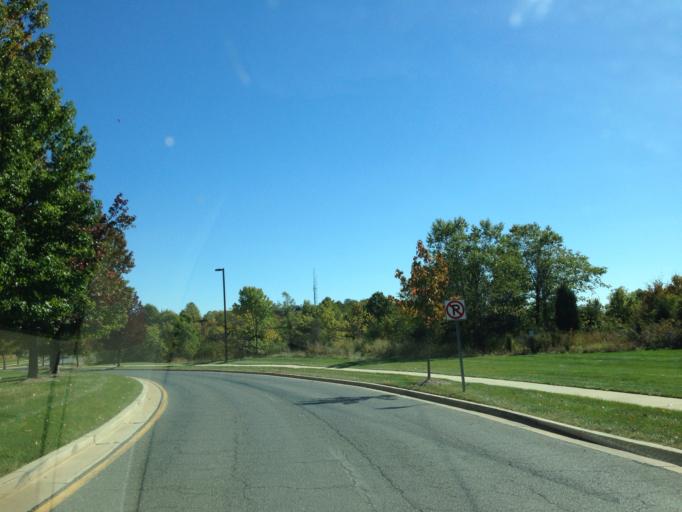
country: US
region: Maryland
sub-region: Montgomery County
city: Germantown
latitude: 39.1906
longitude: -77.2583
